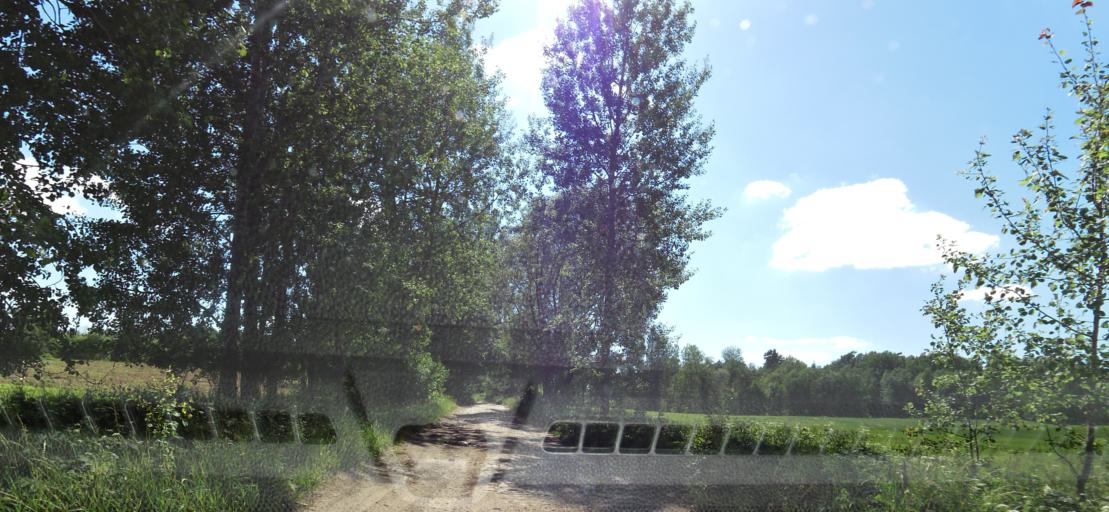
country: LT
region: Vilnius County
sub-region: Vilnius
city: Fabijoniskes
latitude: 54.8413
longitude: 25.3302
